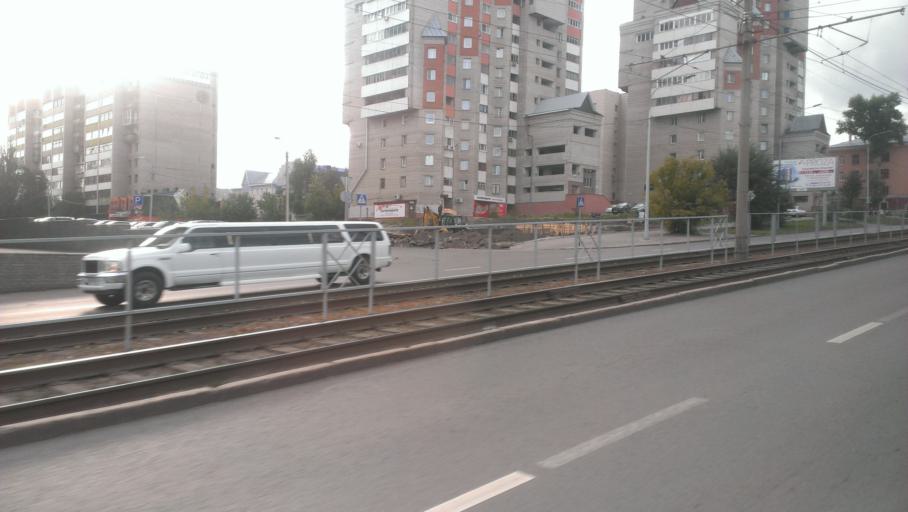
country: RU
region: Altai Krai
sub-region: Gorod Barnaulskiy
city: Barnaul
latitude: 53.3409
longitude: 83.7710
